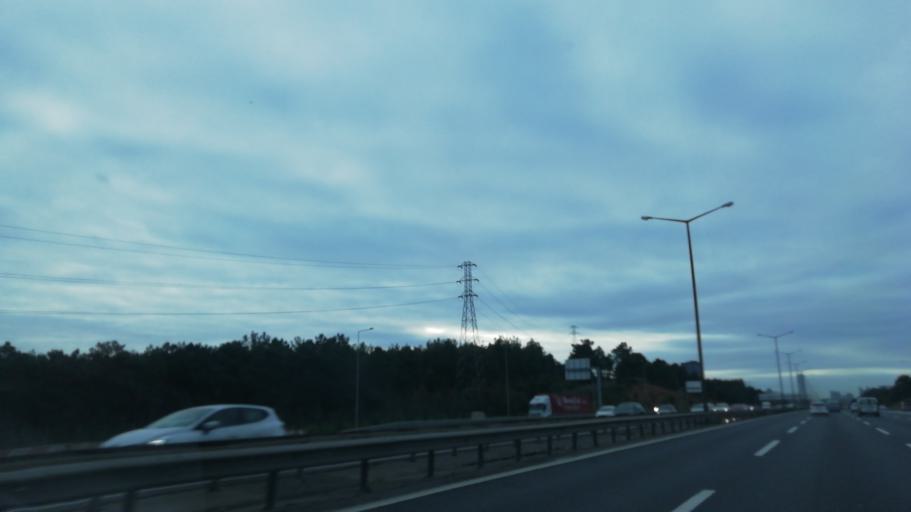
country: TR
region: Istanbul
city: Umraniye
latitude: 41.0444
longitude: 29.1213
